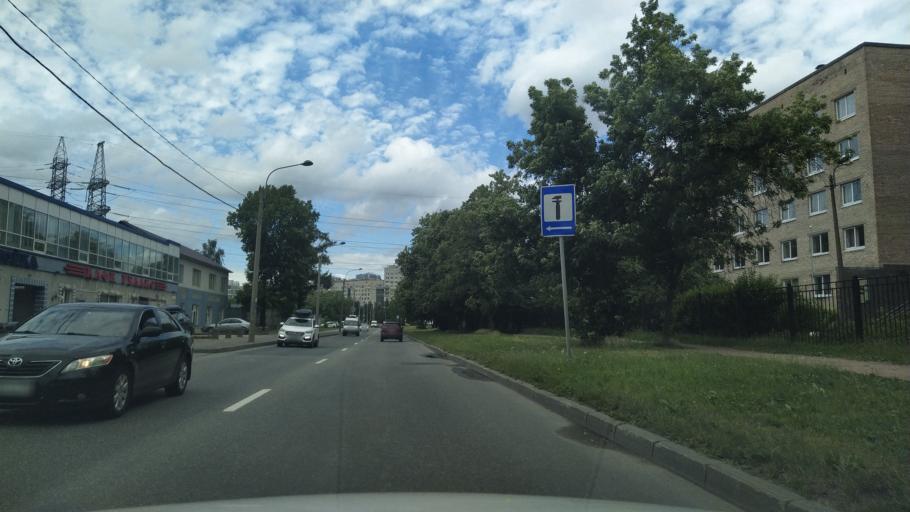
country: RU
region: Leningrad
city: Finlyandskiy
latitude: 59.9760
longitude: 30.3835
